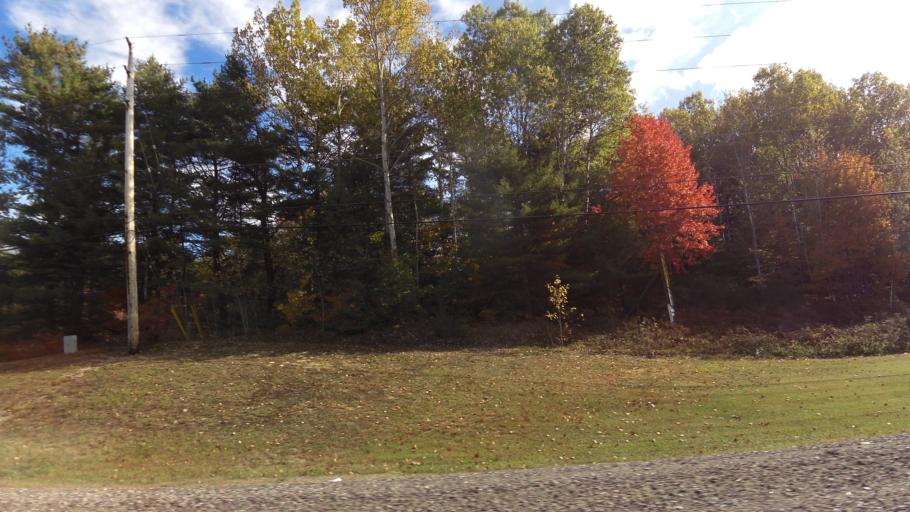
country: CA
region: Ontario
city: Deep River
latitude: 46.0479
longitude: -77.4716
